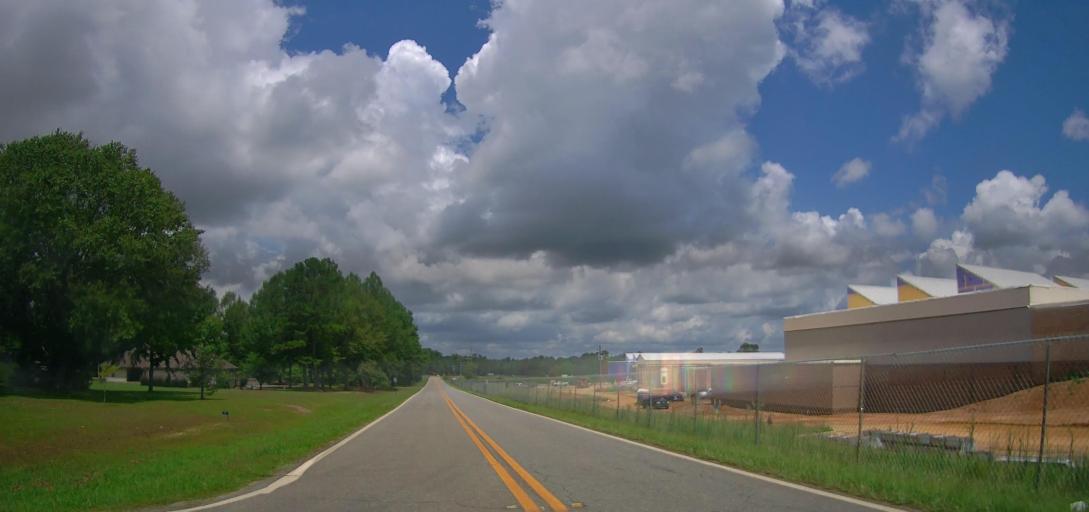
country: US
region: Georgia
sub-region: Pulaski County
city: Hawkinsville
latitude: 32.2830
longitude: -83.4921
